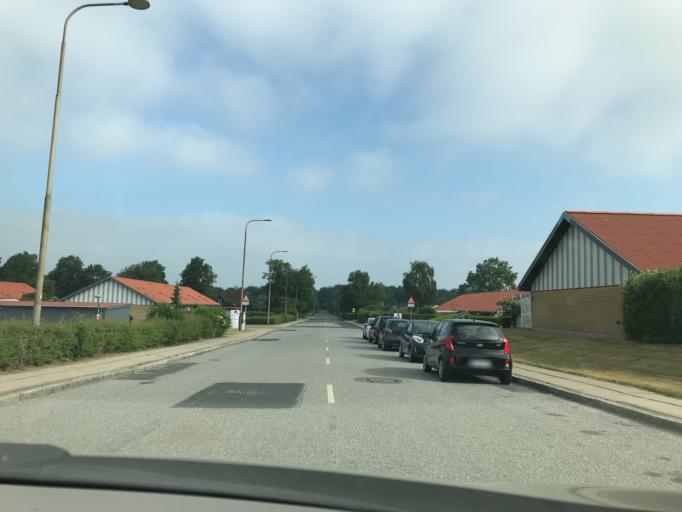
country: DK
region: South Denmark
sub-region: Odense Kommune
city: Bellinge
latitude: 55.3703
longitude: 10.3369
